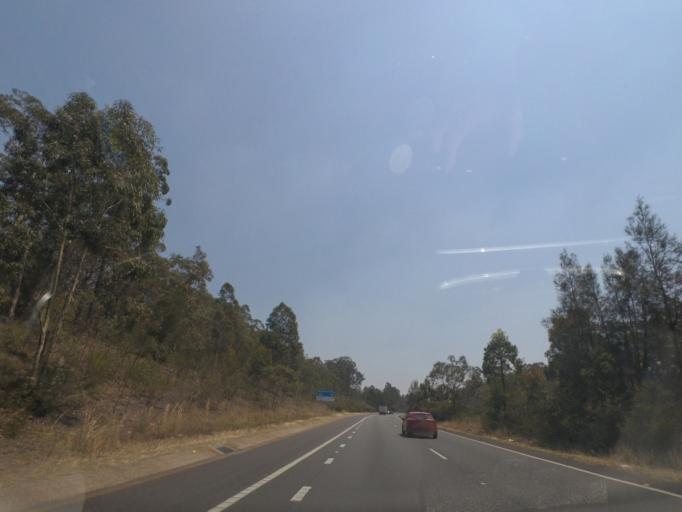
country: AU
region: New South Wales
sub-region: Newcastle
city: Beresfield
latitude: -32.8311
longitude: 151.6339
